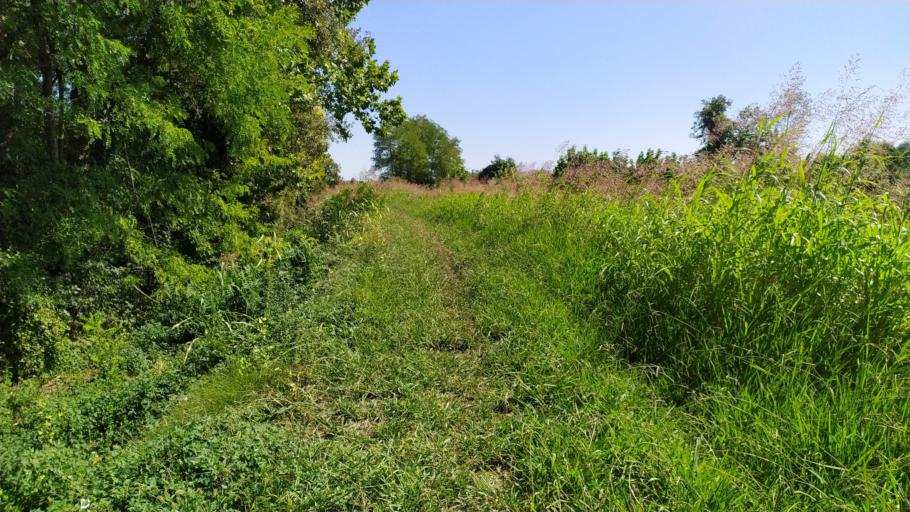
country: IT
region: Friuli Venezia Giulia
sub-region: Provincia di Pordenone
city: Cavolano-Schiavoi
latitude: 45.9376
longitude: 12.4842
